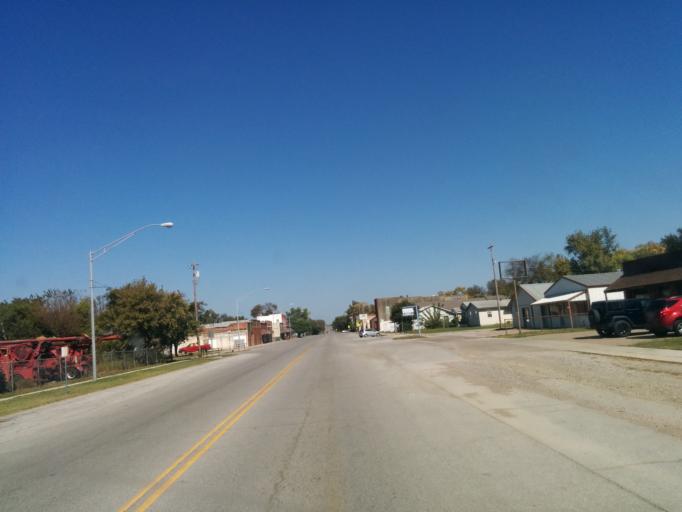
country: US
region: Oklahoma
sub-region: Creek County
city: Mounds
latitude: 35.8747
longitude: -96.0607
